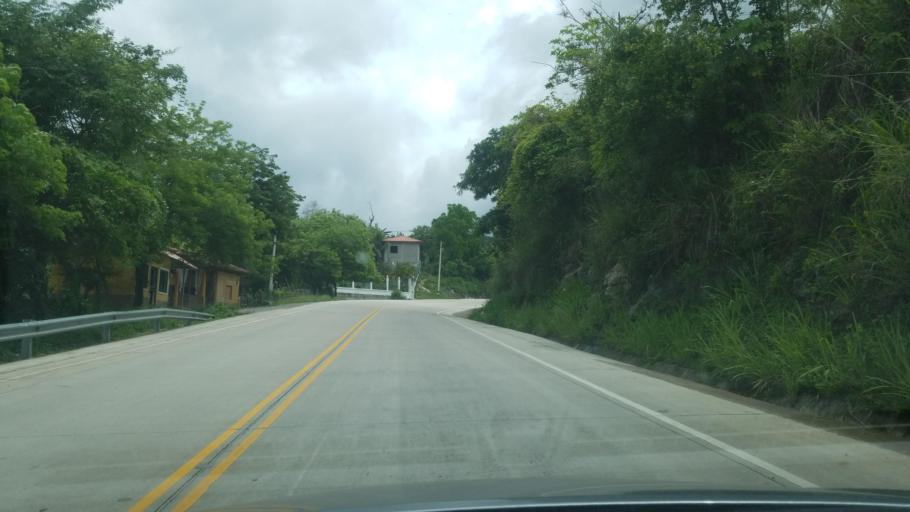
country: HN
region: Copan
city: San Jeronimo
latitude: 14.9862
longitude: -88.8488
